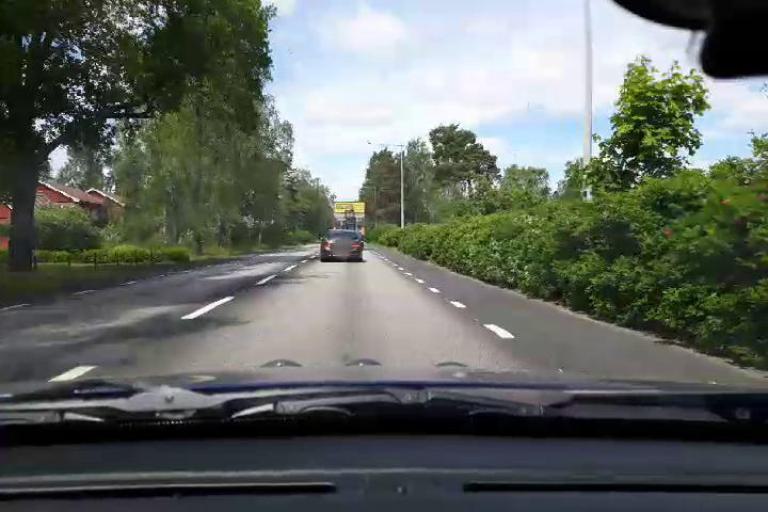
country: SE
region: Uppsala
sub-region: Osthammars Kommun
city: Bjorklinge
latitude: 60.0345
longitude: 17.5520
